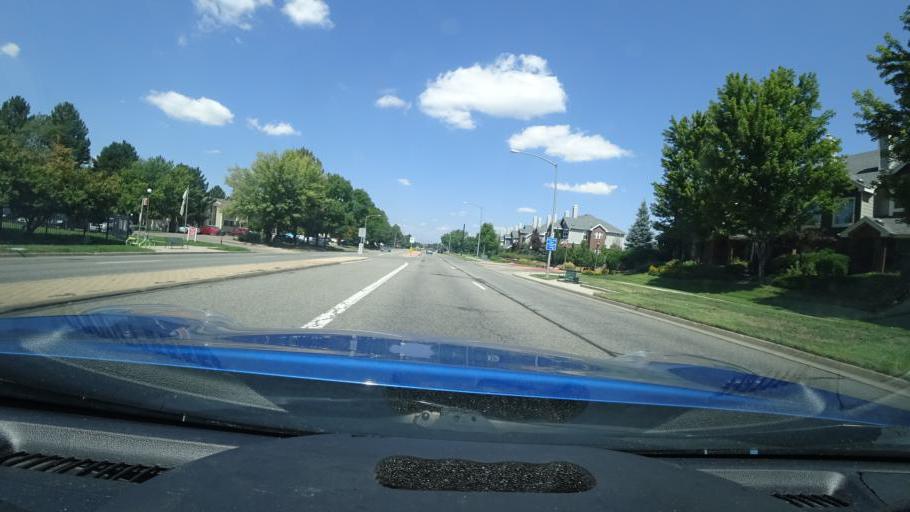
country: US
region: Colorado
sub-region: Arapahoe County
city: Glendale
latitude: 39.7079
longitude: -104.8870
